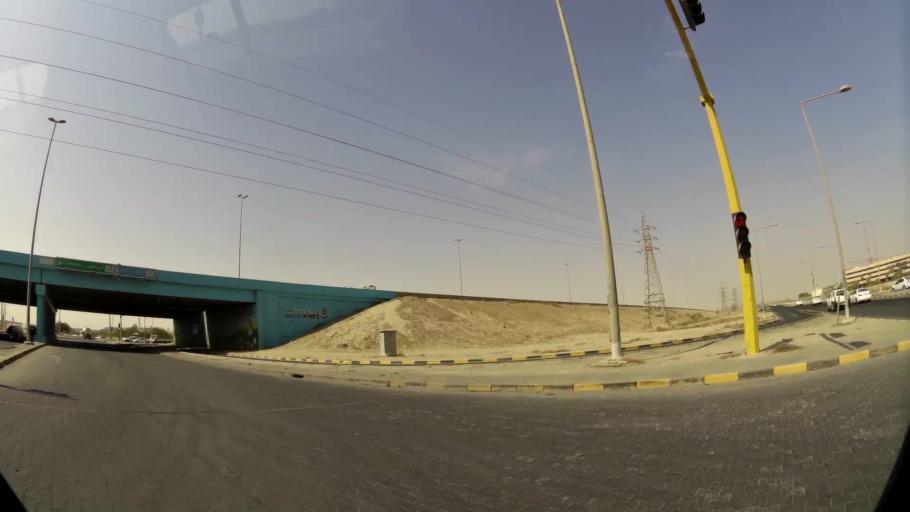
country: KW
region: Al Ahmadi
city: Al Fahahil
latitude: 28.9966
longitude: 48.1437
